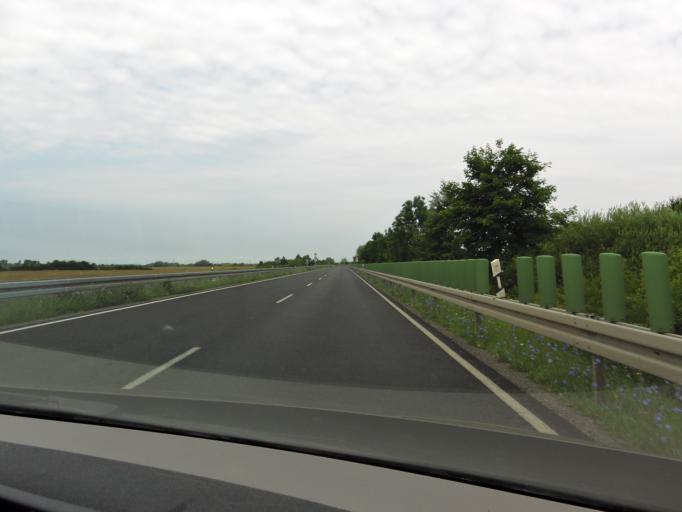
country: DE
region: Saxony-Anhalt
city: Wittenburg
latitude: 51.8310
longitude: 12.6330
